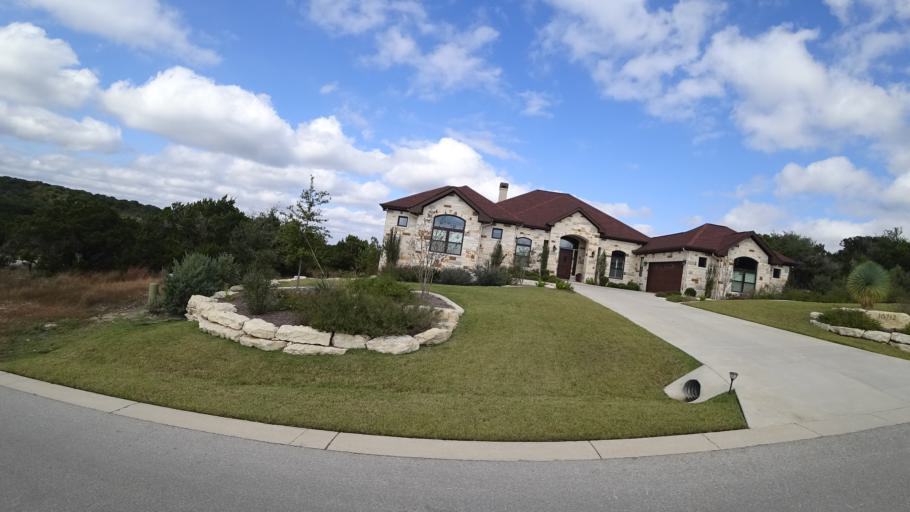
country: US
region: Texas
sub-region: Travis County
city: Bee Cave
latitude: 30.2554
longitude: -97.9281
